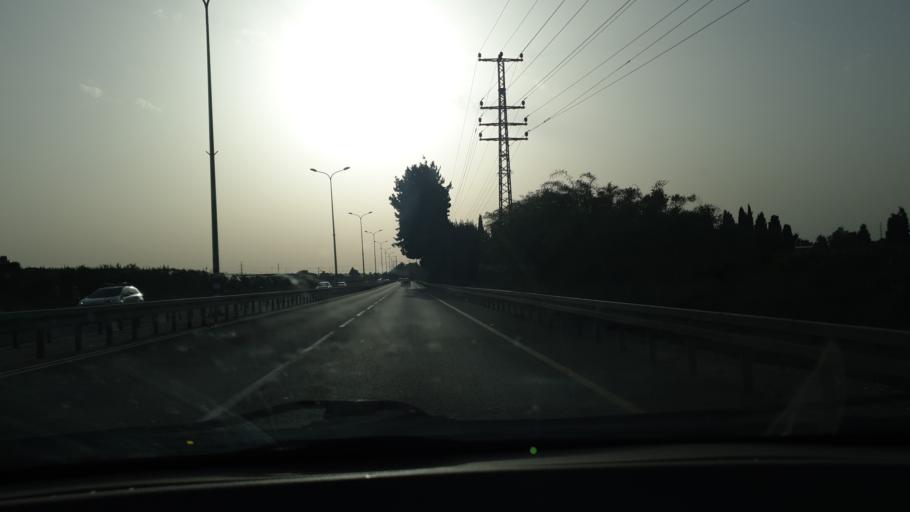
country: IL
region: Central District
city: Tel Mond
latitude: 32.2607
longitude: 34.9110
